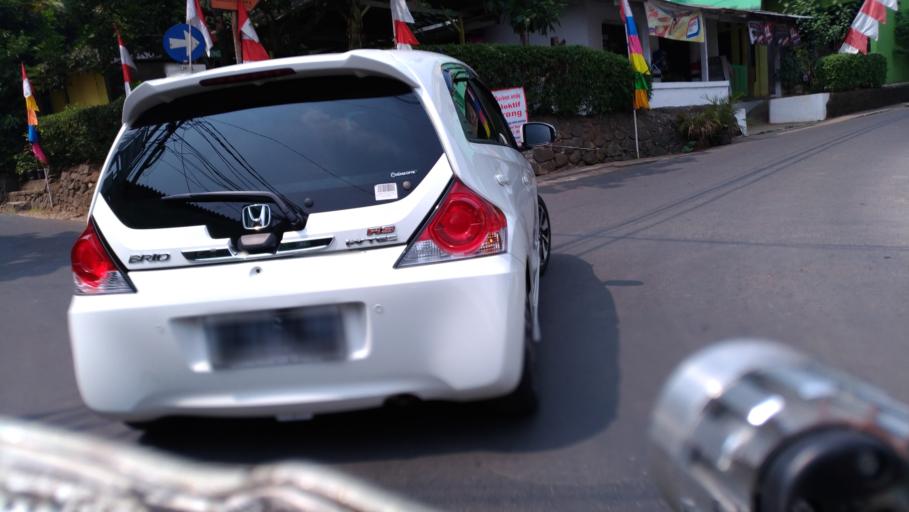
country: ID
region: West Java
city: Cileungsir
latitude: -6.3181
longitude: 106.9017
